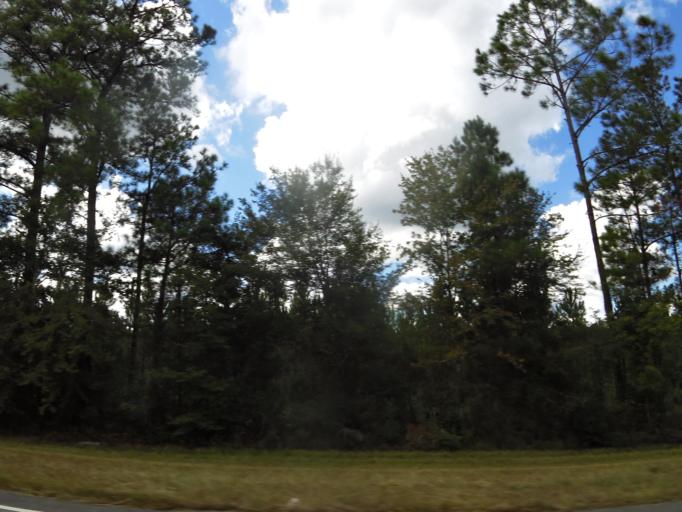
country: US
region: Georgia
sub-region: Charlton County
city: Folkston
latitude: 30.9077
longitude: -82.0184
